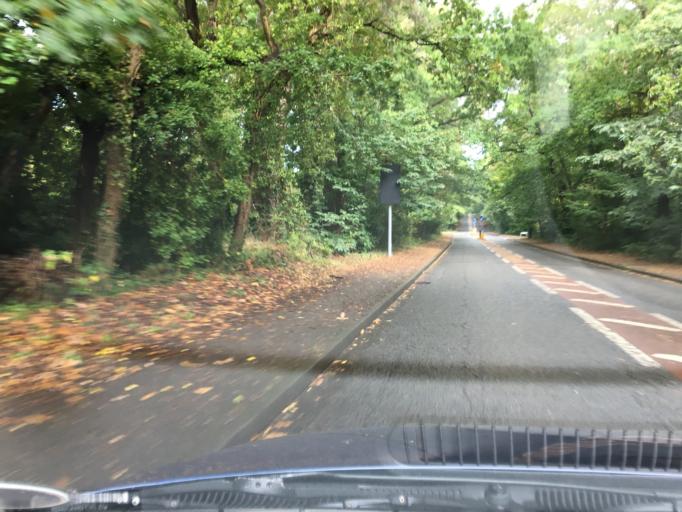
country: GB
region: England
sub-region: Bracknell Forest
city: Crowthorne
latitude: 51.3776
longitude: -0.8049
